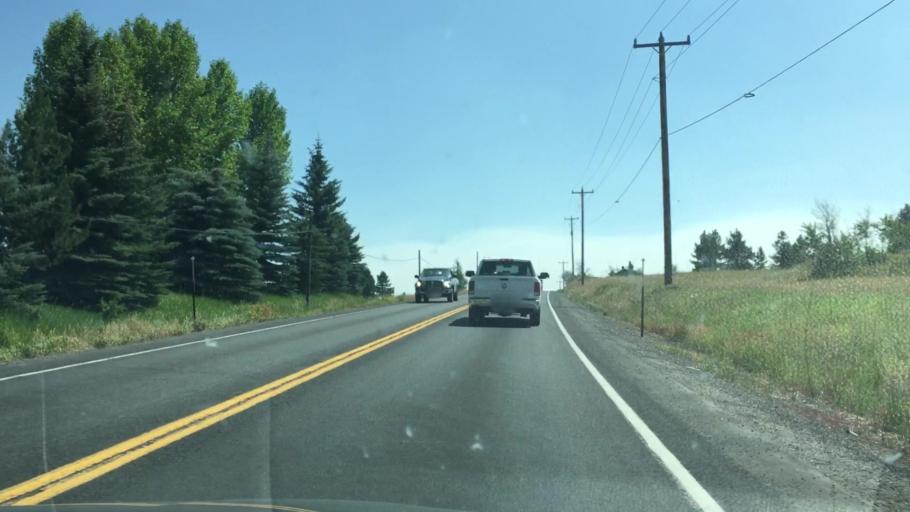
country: US
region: Idaho
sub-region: Valley County
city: McCall
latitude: 44.8822
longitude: -116.0907
